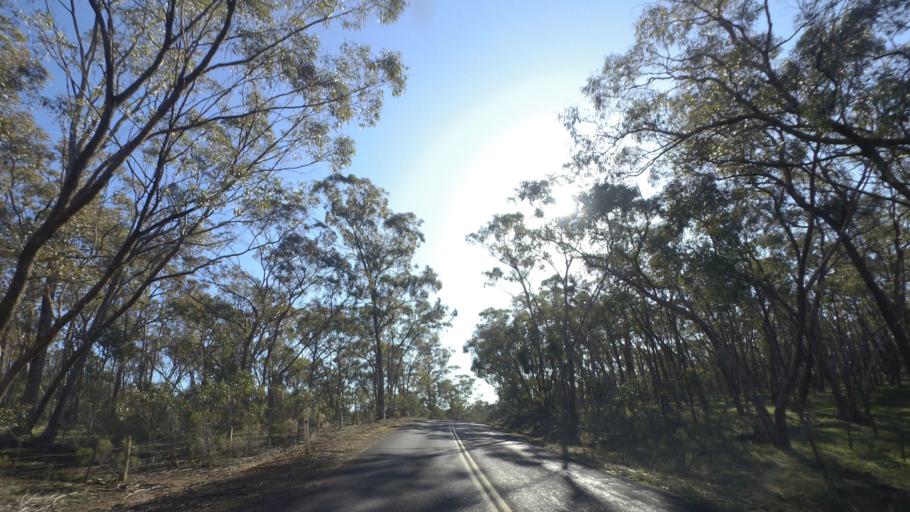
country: AU
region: Victoria
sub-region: Greater Bendigo
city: Kangaroo Flat
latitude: -36.8833
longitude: 144.2829
